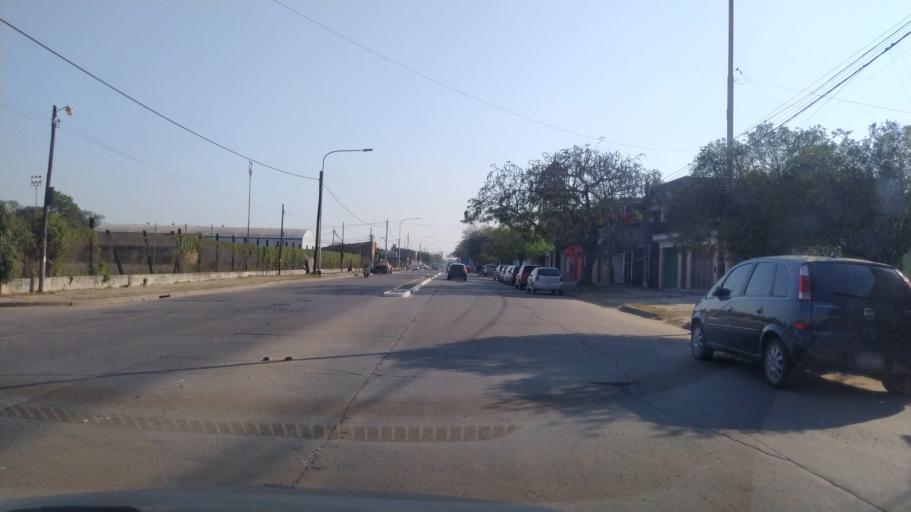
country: AR
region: Corrientes
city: Corrientes
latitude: -27.4853
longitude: -58.8159
